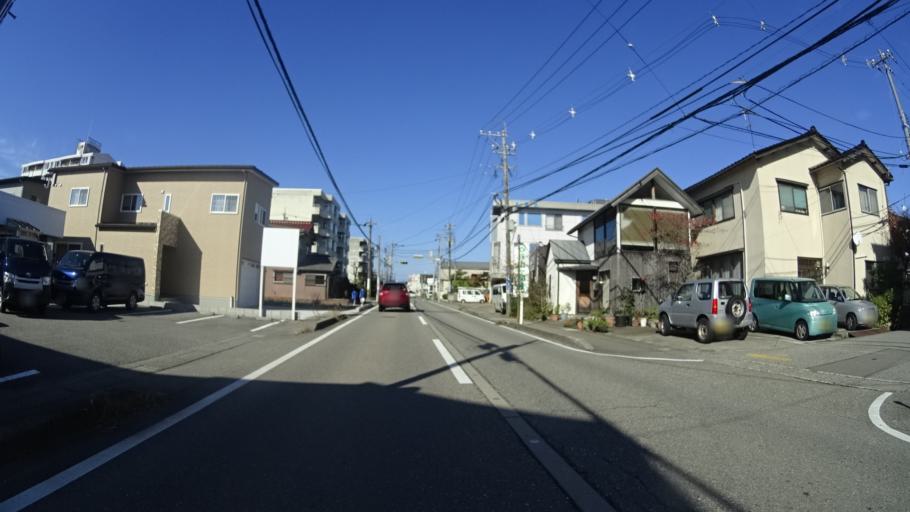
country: JP
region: Ishikawa
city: Kanazawa-shi
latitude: 36.5983
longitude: 136.6086
